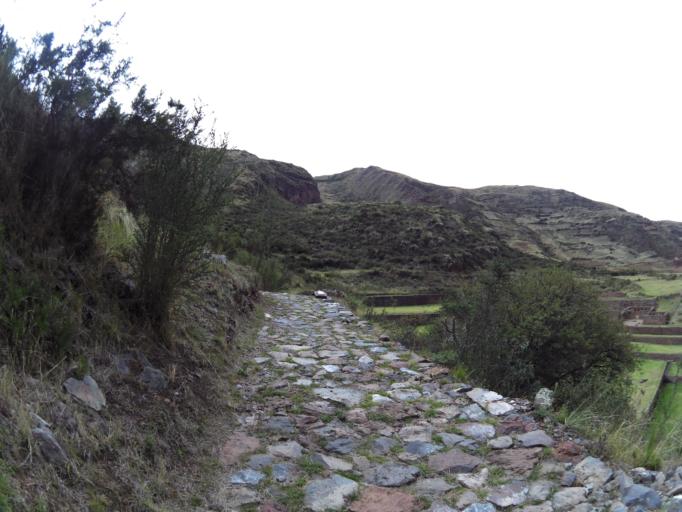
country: PE
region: Cusco
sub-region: Provincia de Quispicanchis
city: Oropesa
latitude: -13.5693
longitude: -71.7826
